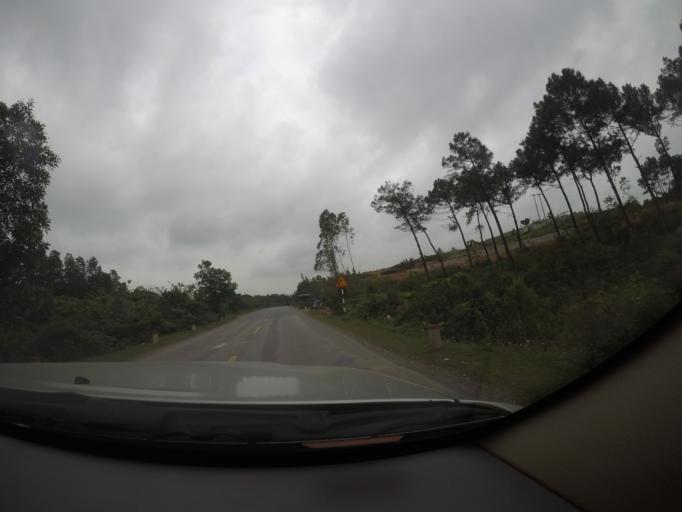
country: VN
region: Quang Binh
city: Quan Hau
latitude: 17.3551
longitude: 106.6241
